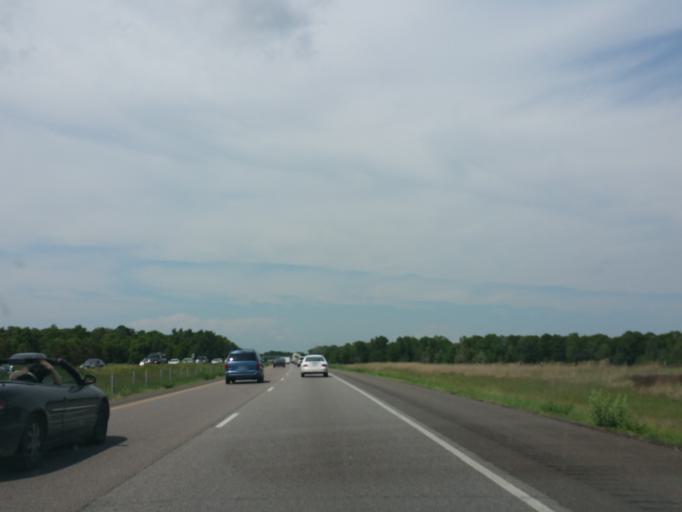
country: US
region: Minnesota
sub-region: Chisago County
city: Stacy
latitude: 45.4402
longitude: -92.9889
